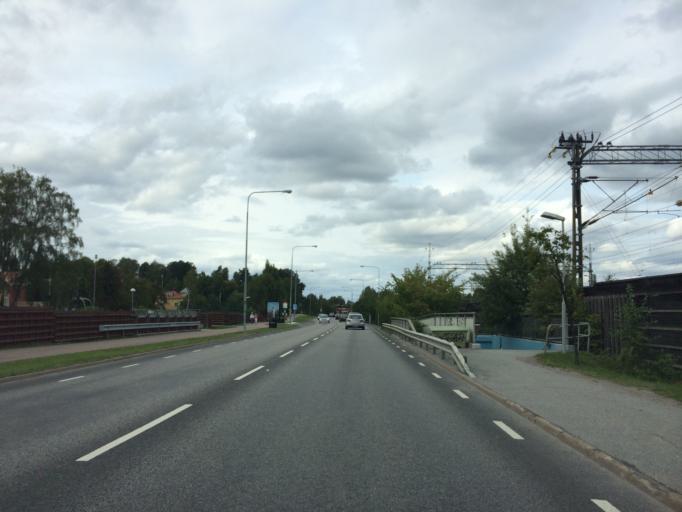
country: SE
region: Stockholm
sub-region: Sollentuna Kommun
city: Sollentuna
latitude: 59.4525
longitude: 17.9253
